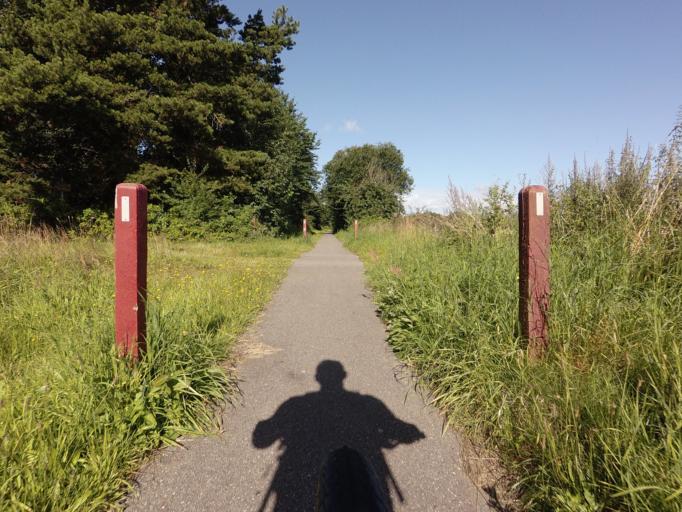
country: DK
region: Central Jutland
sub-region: Horsens Kommune
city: Horsens
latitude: 55.9519
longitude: 9.7787
